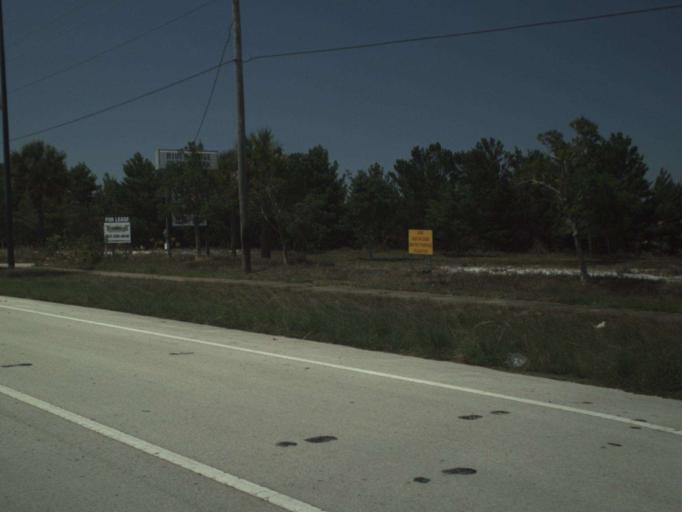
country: US
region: Florida
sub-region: Saint Lucie County
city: Fort Pierce North
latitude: 27.4713
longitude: -80.3344
